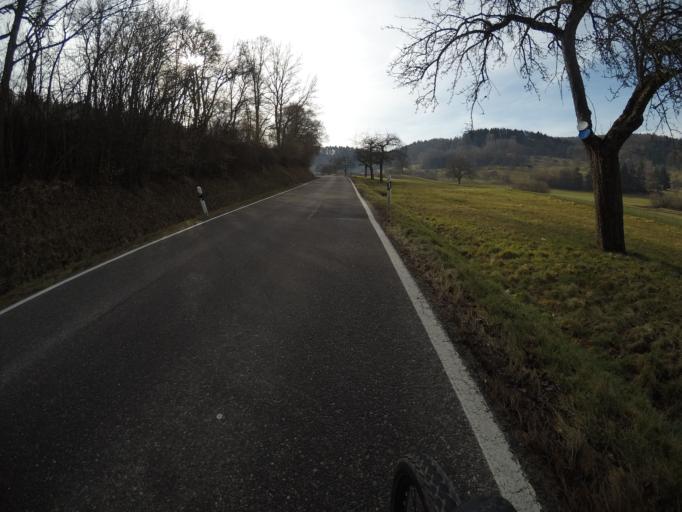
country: DE
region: Baden-Wuerttemberg
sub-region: Karlsruhe Region
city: Calw
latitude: 48.6872
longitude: 8.7685
